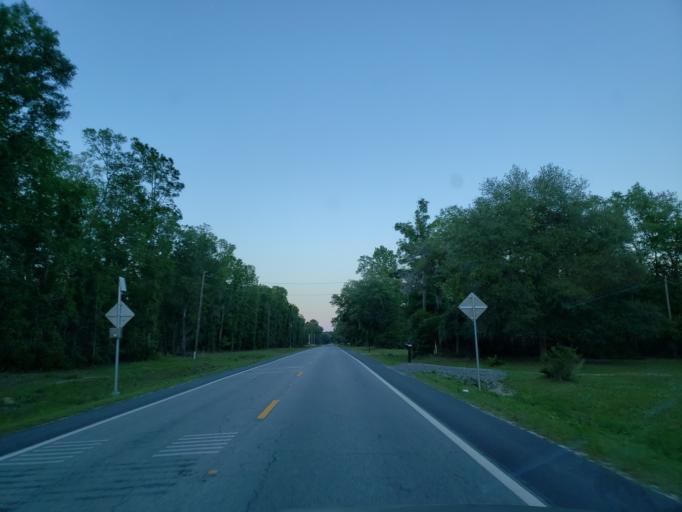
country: US
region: Florida
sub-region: Hamilton County
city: Jasper
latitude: 30.5559
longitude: -83.0978
